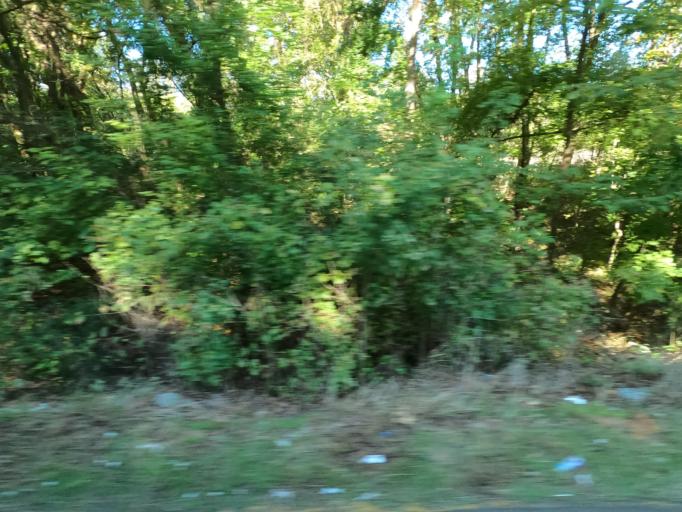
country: US
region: Tennessee
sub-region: Tipton County
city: Munford
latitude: 35.4319
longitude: -89.8049
